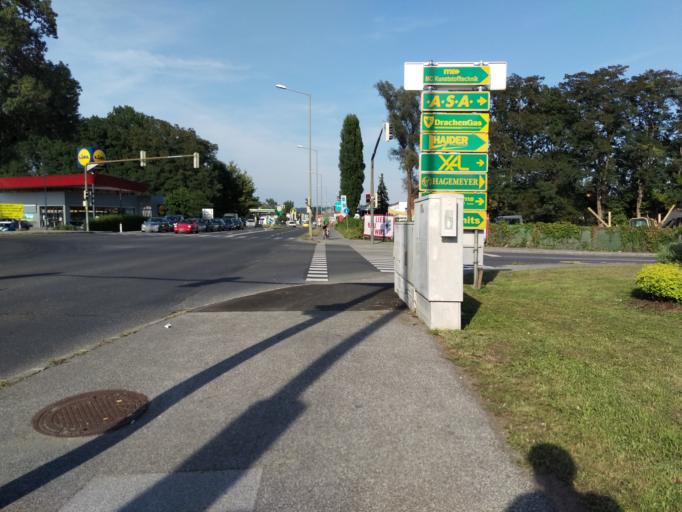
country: AT
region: Styria
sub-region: Politischer Bezirk Graz-Umgebung
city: Feldkirchen bei Graz
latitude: 47.0322
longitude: 15.4408
